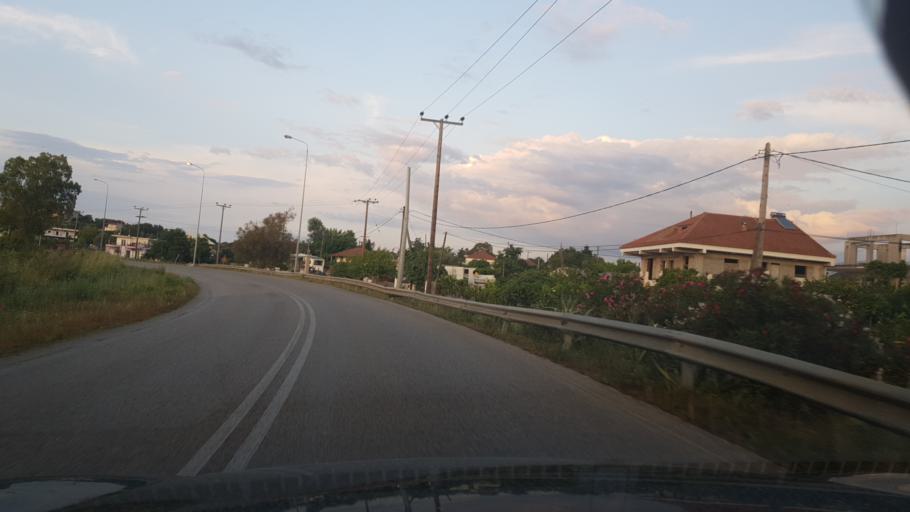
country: GR
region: West Greece
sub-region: Nomos Aitolias kai Akarnanias
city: Vonitsa
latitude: 38.8644
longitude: 20.8006
